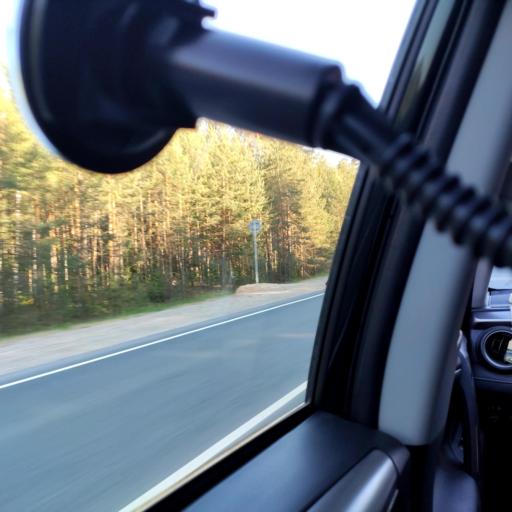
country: RU
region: Mariy-El
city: Suslonger
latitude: 56.2468
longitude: 48.2318
